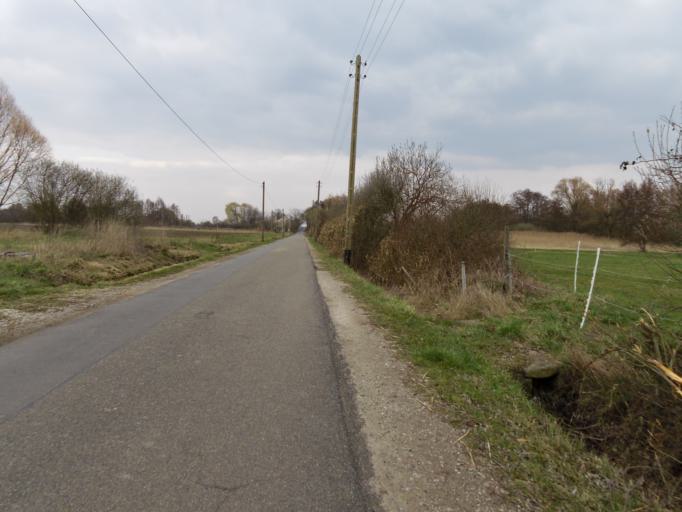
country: DE
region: Rheinland-Pfalz
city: Erpolzheim
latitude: 49.4778
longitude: 8.2298
